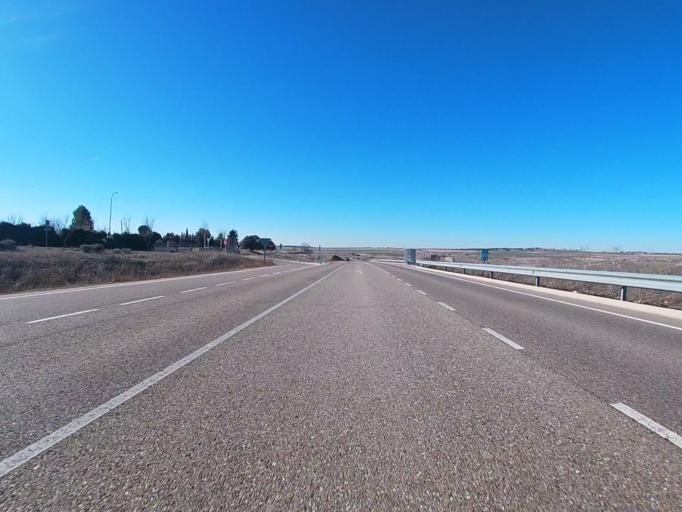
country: ES
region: Castille and Leon
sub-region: Provincia de Salamanca
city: Juzbado
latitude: 41.0797
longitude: -5.8609
